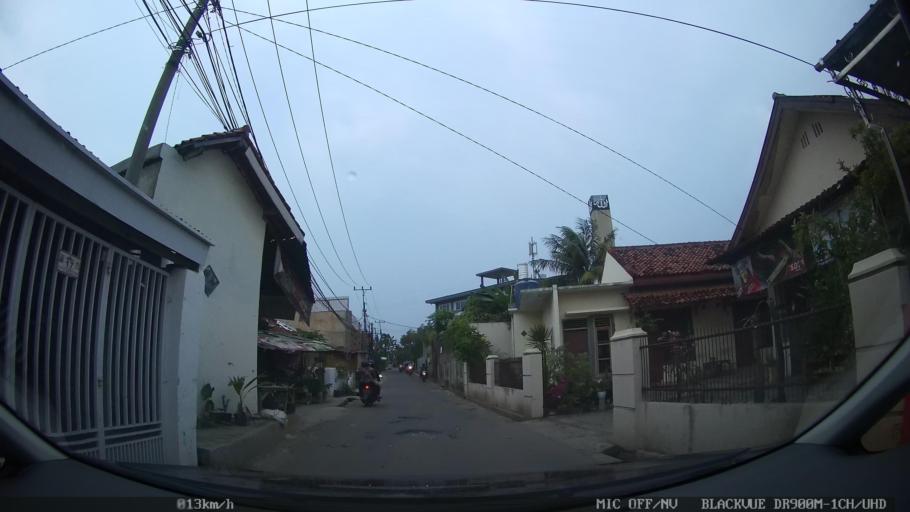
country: ID
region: Lampung
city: Kedaton
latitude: -5.4027
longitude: 105.2733
